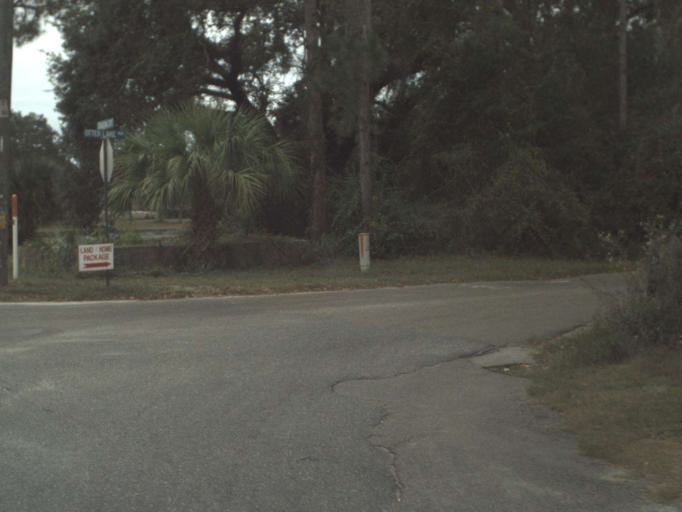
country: US
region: Florida
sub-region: Wakulla County
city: Crawfordville
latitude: 30.0295
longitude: -84.3904
